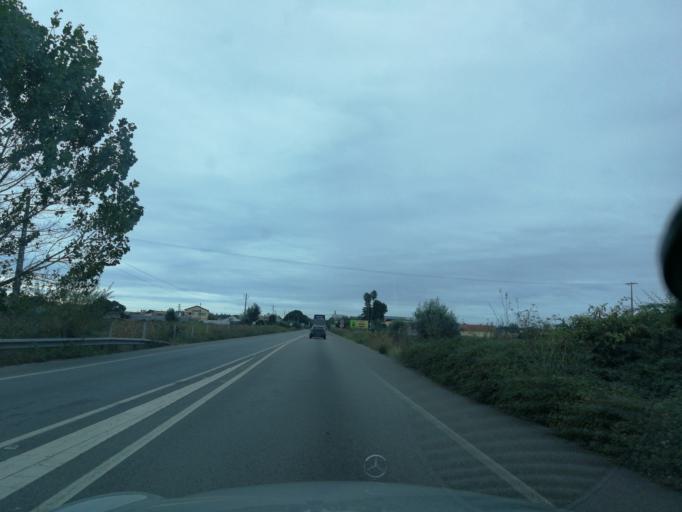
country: PT
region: Aveiro
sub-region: Agueda
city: Valongo
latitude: 40.6168
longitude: -8.4632
